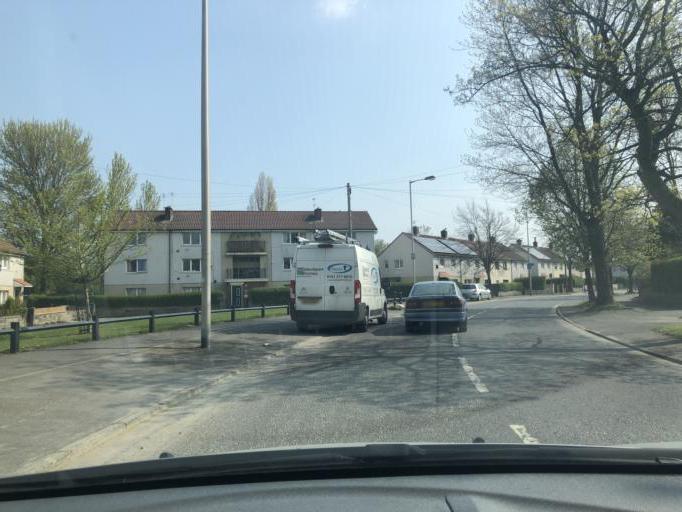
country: GB
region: England
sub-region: Borough of Stockport
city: Bredbury
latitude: 53.4301
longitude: -2.1304
